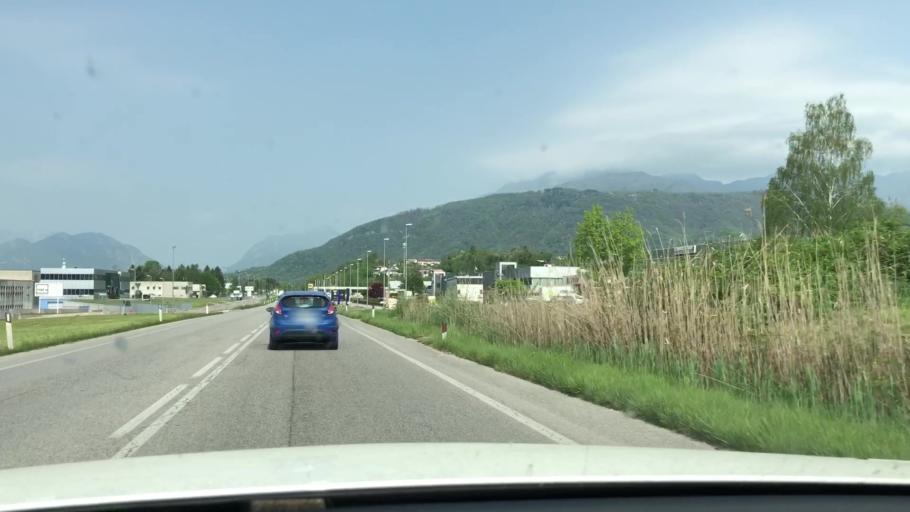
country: IT
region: Friuli Venezia Giulia
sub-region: Provincia di Udine
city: Magnano in Riviera
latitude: 46.2032
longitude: 13.1900
